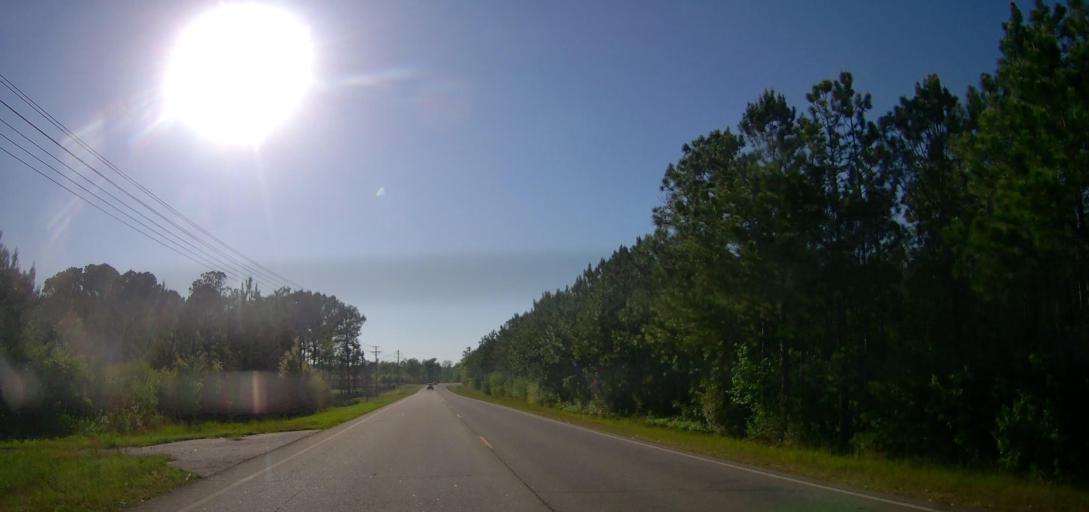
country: US
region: Georgia
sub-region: Ben Hill County
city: Fitzgerald
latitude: 31.6941
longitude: -83.2927
